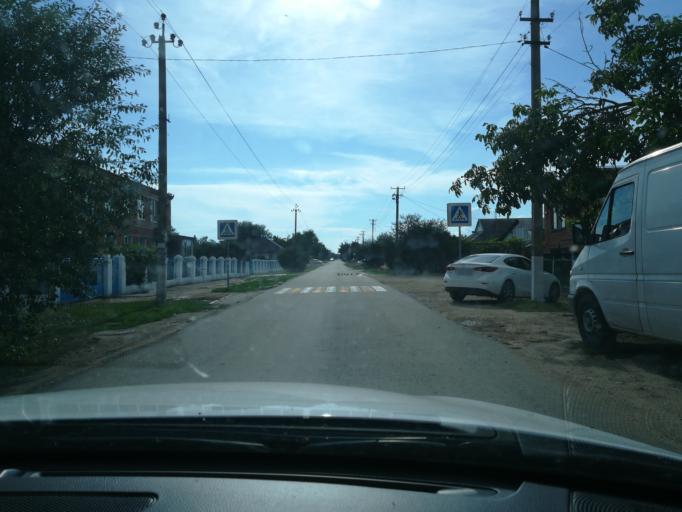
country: RU
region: Krasnodarskiy
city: Strelka
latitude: 45.1728
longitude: 37.2715
